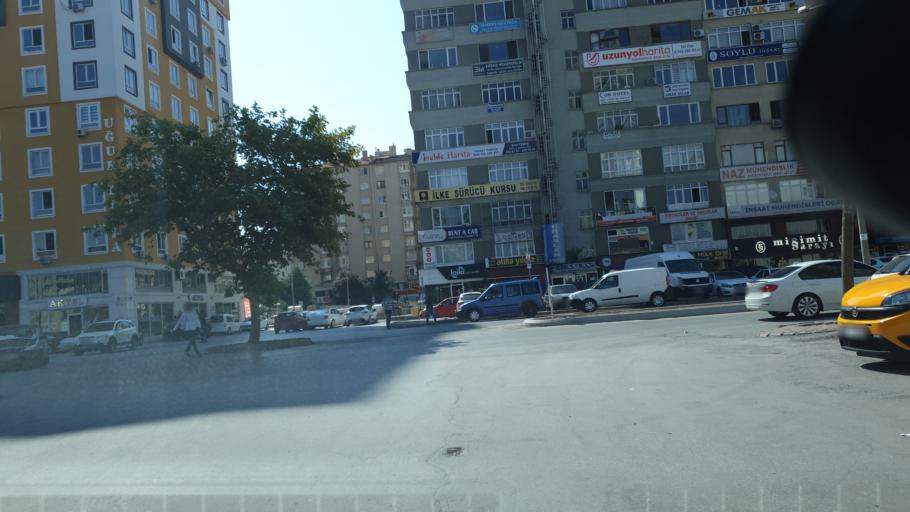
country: TR
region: Kayseri
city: Kayseri
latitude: 38.7251
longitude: 35.4922
